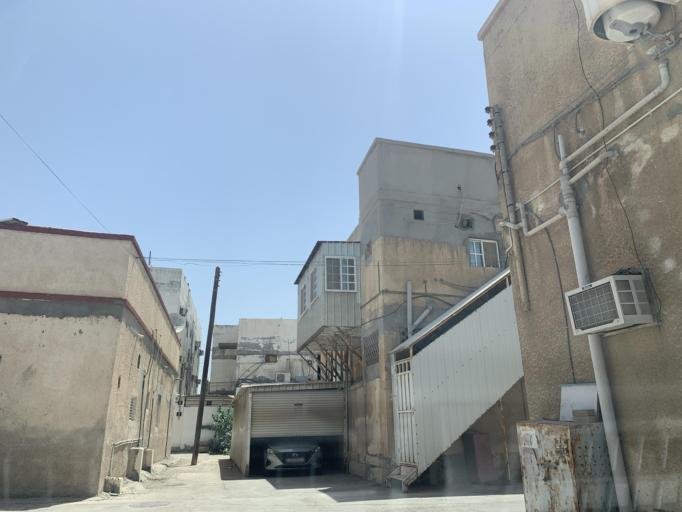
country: BH
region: Northern
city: Sitrah
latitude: 26.1595
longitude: 50.6197
